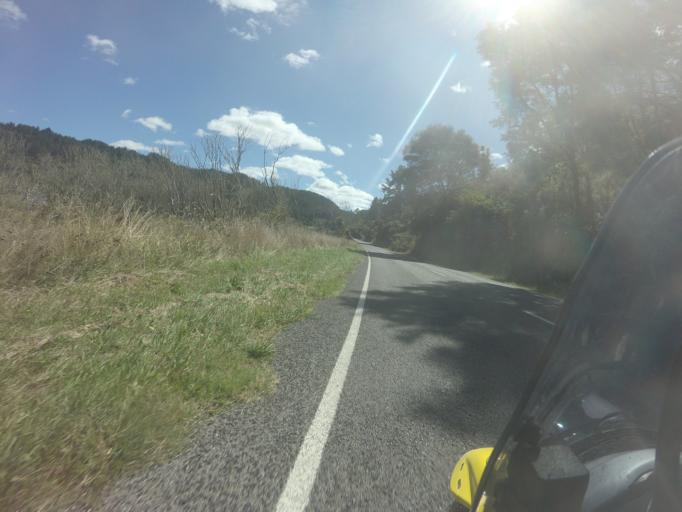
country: NZ
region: Bay of Plenty
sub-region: Kawerau District
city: Kawerau
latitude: -38.1807
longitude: 176.8350
